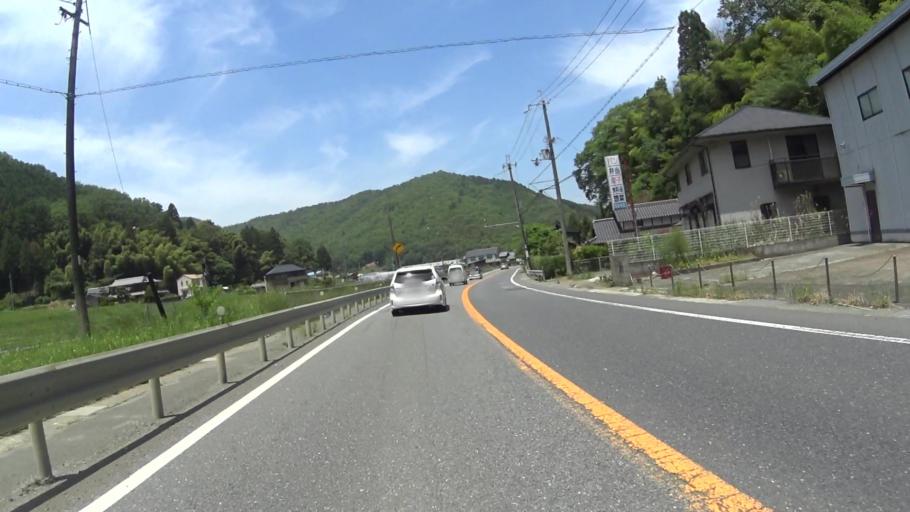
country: JP
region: Kyoto
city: Kameoka
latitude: 35.1369
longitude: 135.4257
